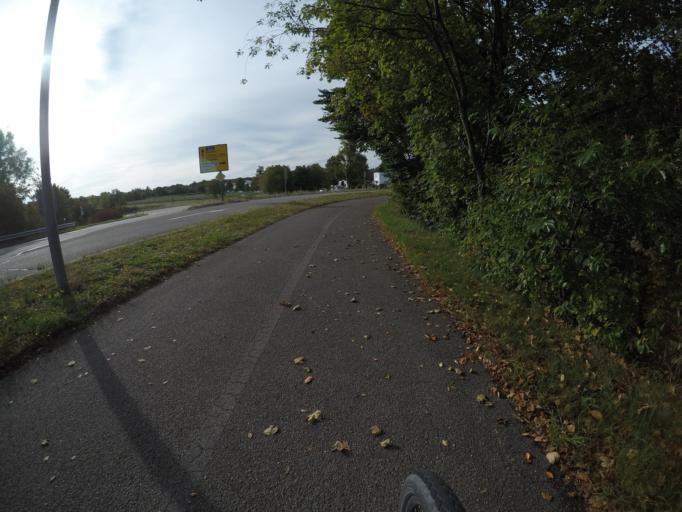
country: DE
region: Baden-Wuerttemberg
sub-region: Karlsruhe Region
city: Oftersheim
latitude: 49.3623
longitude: 8.5832
